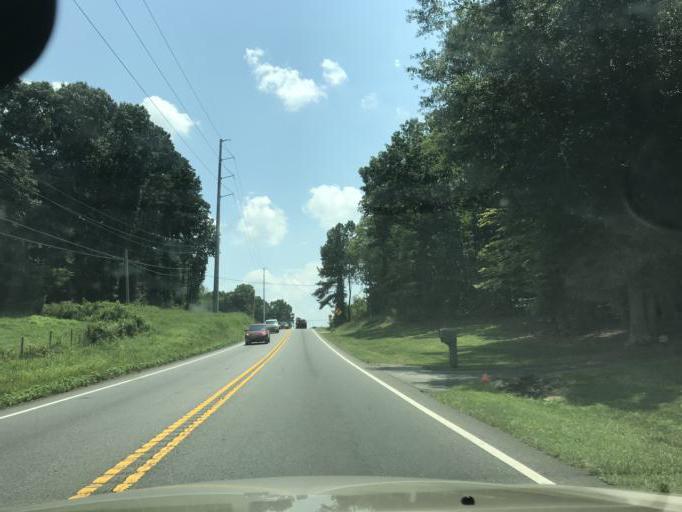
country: US
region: Georgia
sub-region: Forsyth County
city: Cumming
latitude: 34.2854
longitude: -84.1274
